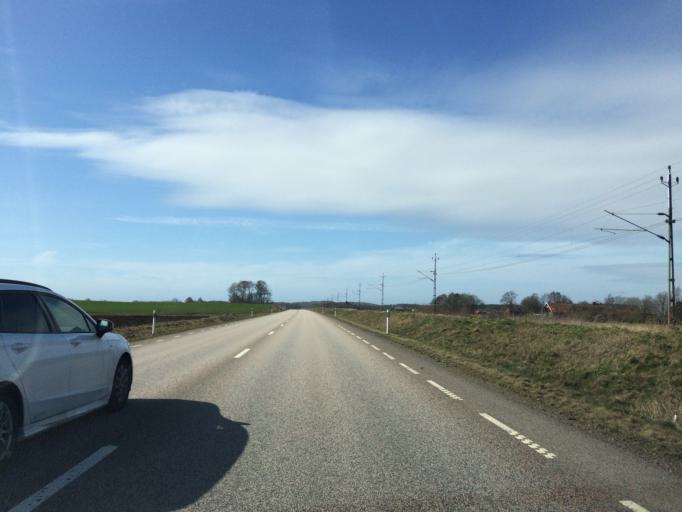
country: SE
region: Halland
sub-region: Laholms Kommun
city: Veinge
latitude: 56.5419
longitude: 13.1404
